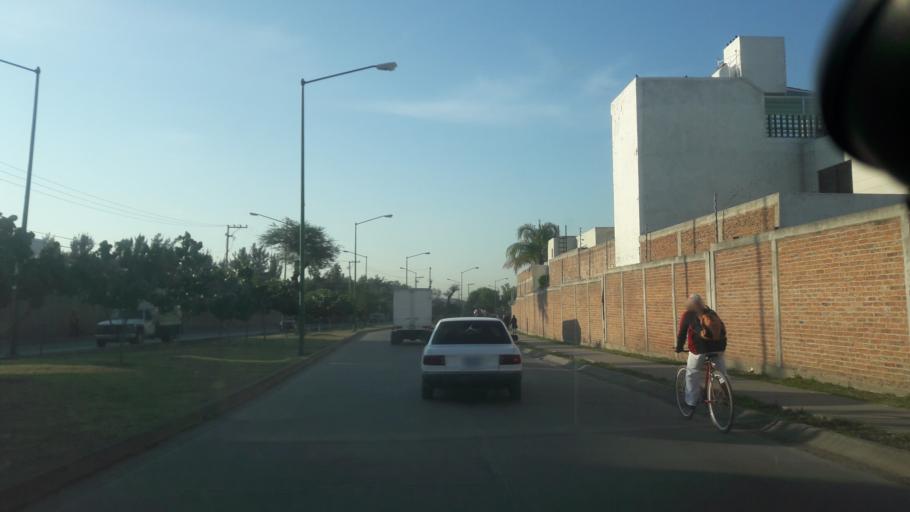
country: MX
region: Guanajuato
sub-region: Leon
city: Medina
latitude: 21.1614
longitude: -101.6425
